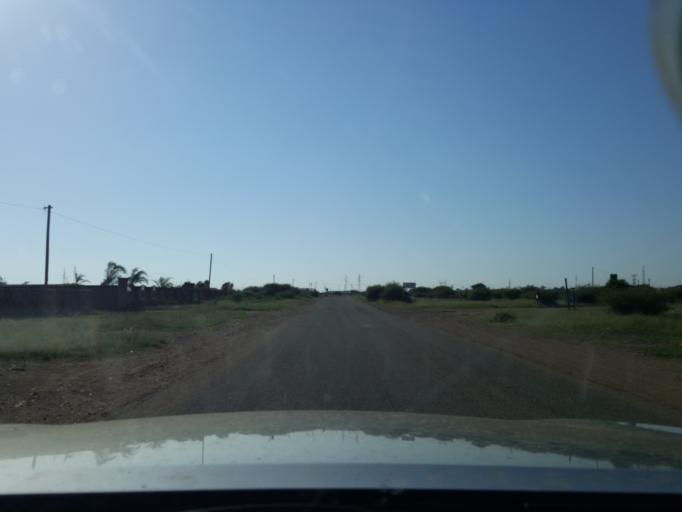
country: ZA
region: North-West
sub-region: Ngaka Modiri Molema District Municipality
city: Mahikeng
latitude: -25.8374
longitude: 25.6692
